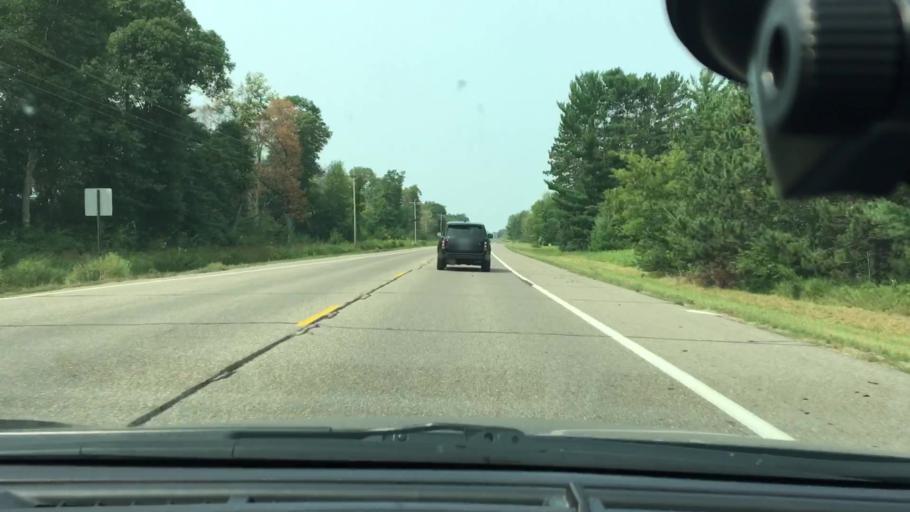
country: US
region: Minnesota
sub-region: Crow Wing County
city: Brainerd
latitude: 46.3984
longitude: -94.2062
